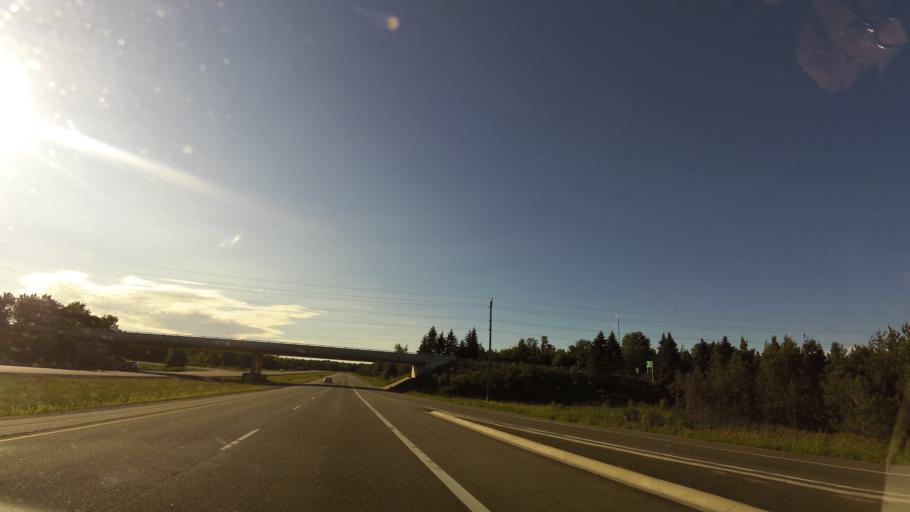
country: CA
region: Ontario
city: Barrie
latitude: 44.5226
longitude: -79.7391
